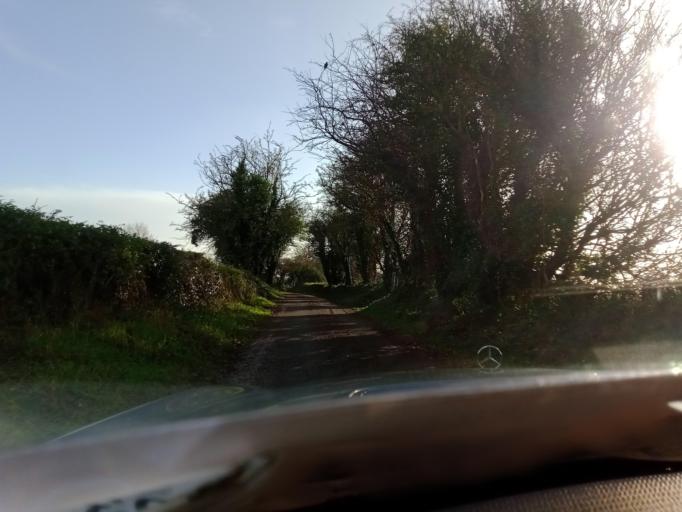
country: IE
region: Leinster
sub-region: Kilkenny
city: Mooncoin
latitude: 52.3195
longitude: -7.2839
